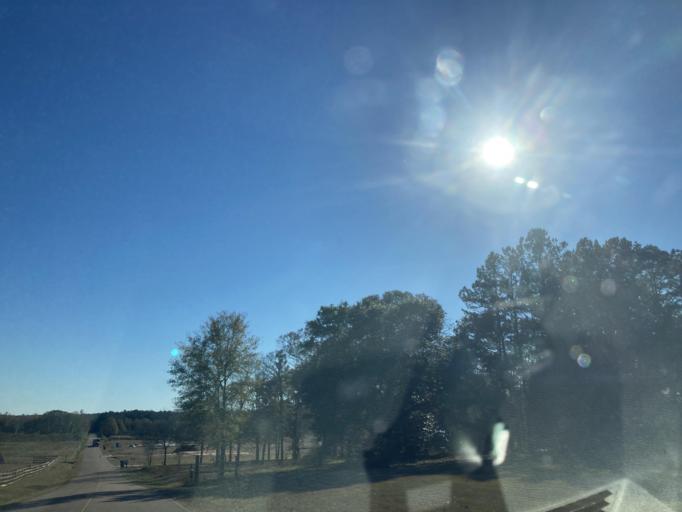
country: US
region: Mississippi
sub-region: Lamar County
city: Sumrall
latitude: 31.3887
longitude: -89.6075
